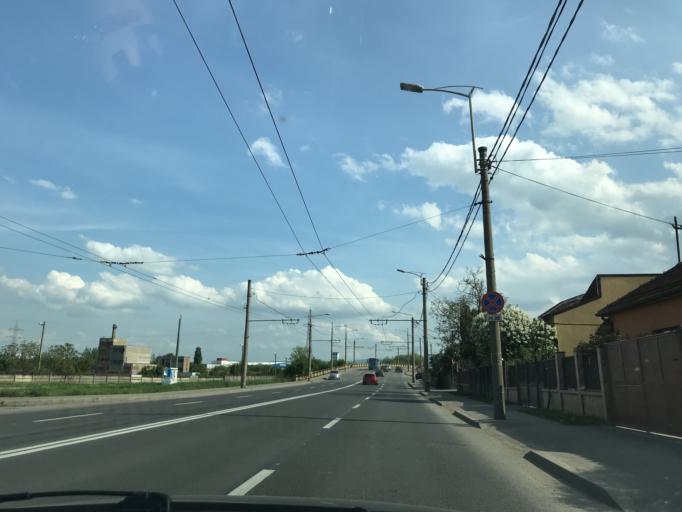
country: RO
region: Cluj
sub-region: Municipiul Cluj-Napoca
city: Cluj-Napoca
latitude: 46.7942
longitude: 23.6145
